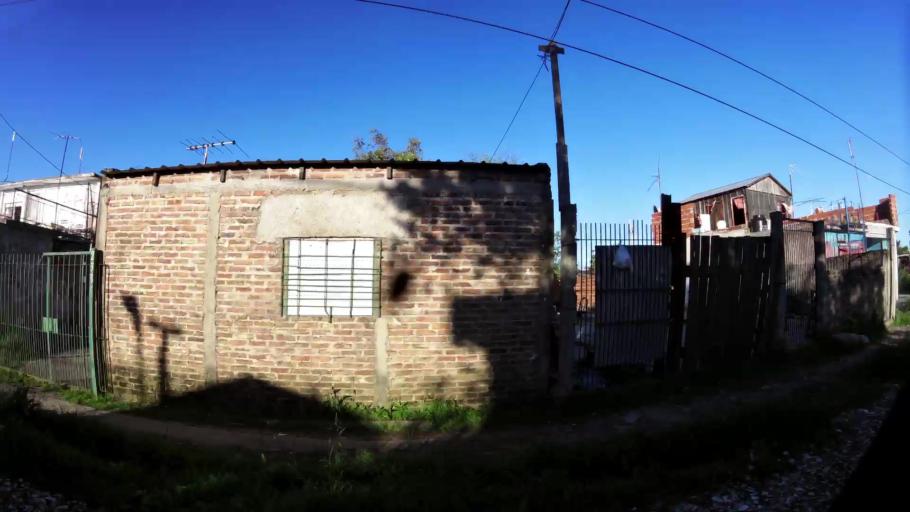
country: AR
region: Buenos Aires
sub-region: Partido de Almirante Brown
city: Adrogue
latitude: -34.7715
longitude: -58.3300
